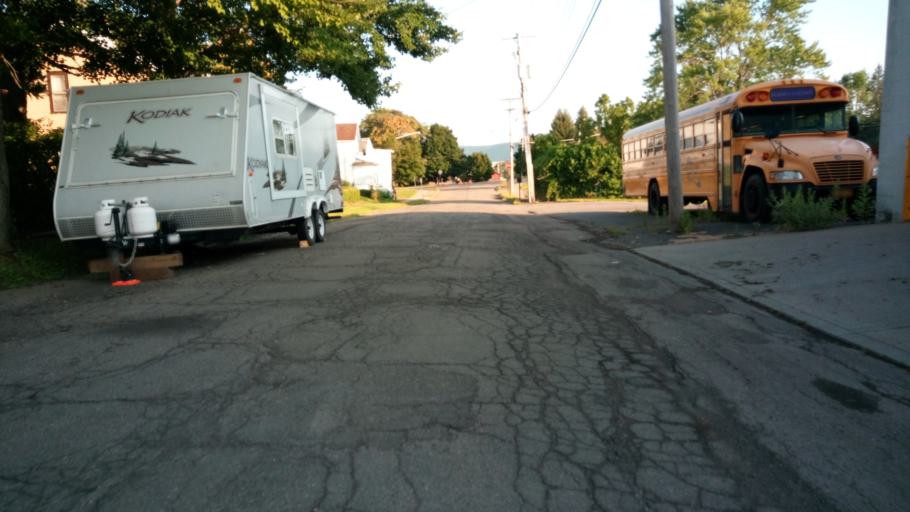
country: US
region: New York
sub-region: Chemung County
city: Elmira
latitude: 42.1011
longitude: -76.8109
